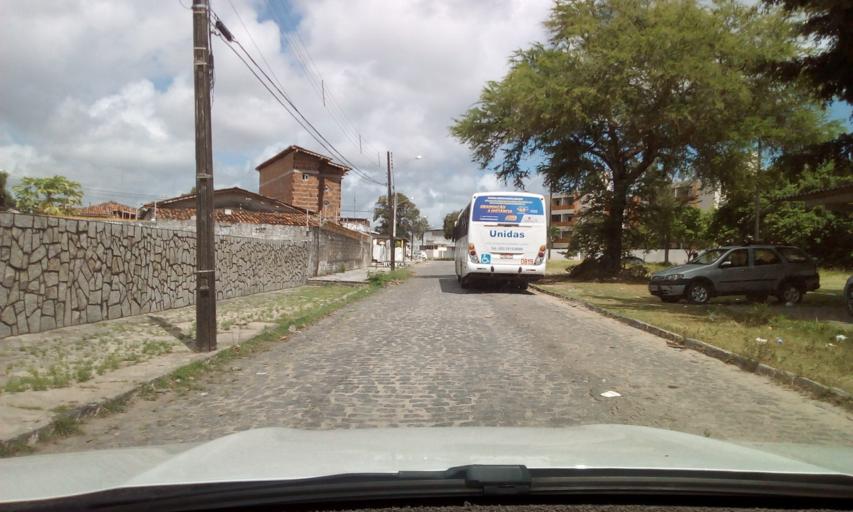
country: BR
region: Paraiba
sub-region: Joao Pessoa
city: Joao Pessoa
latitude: -7.1680
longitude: -34.8501
